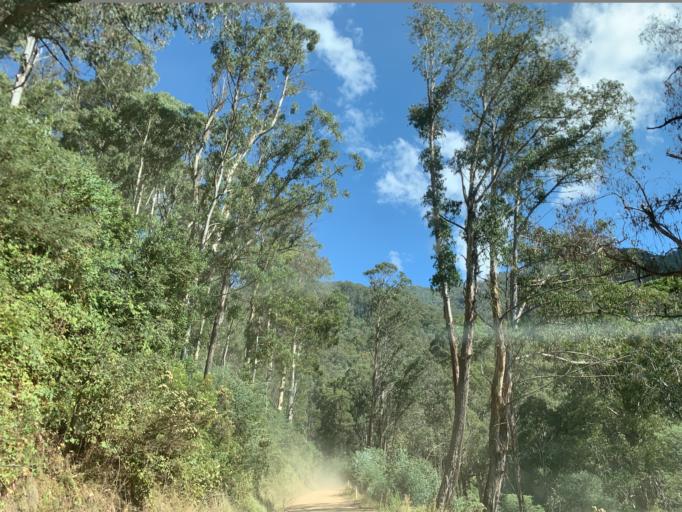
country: AU
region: Victoria
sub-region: Mansfield
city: Mansfield
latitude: -37.1035
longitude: 146.5020
